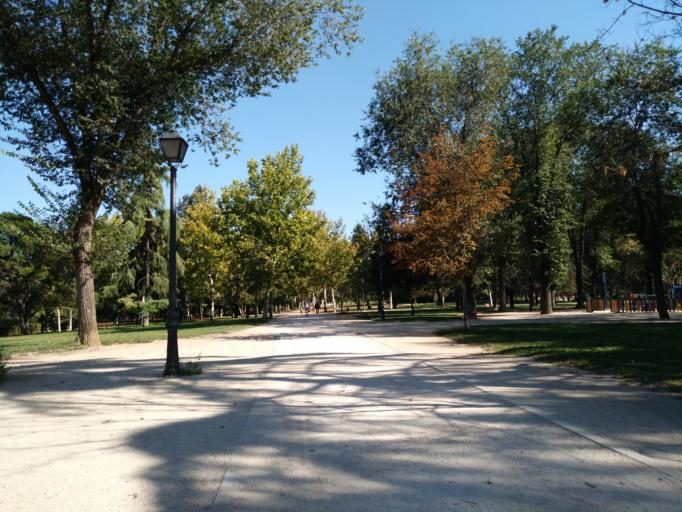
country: ES
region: Madrid
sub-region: Provincia de Madrid
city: Carabanchel
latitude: 40.3815
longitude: -3.7221
